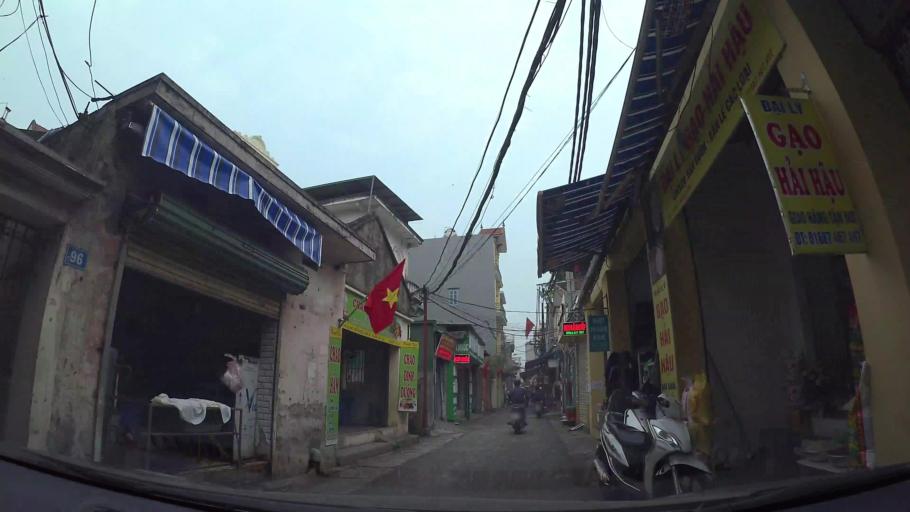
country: VN
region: Ha Noi
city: Van Dien
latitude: 20.9715
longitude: 105.8691
